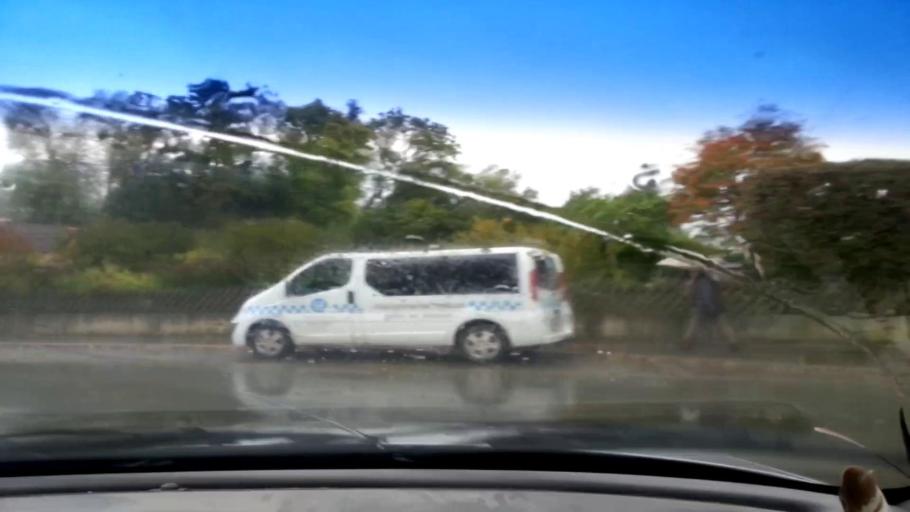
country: DE
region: Bavaria
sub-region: Upper Franconia
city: Schesslitz
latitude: 49.9626
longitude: 10.9966
